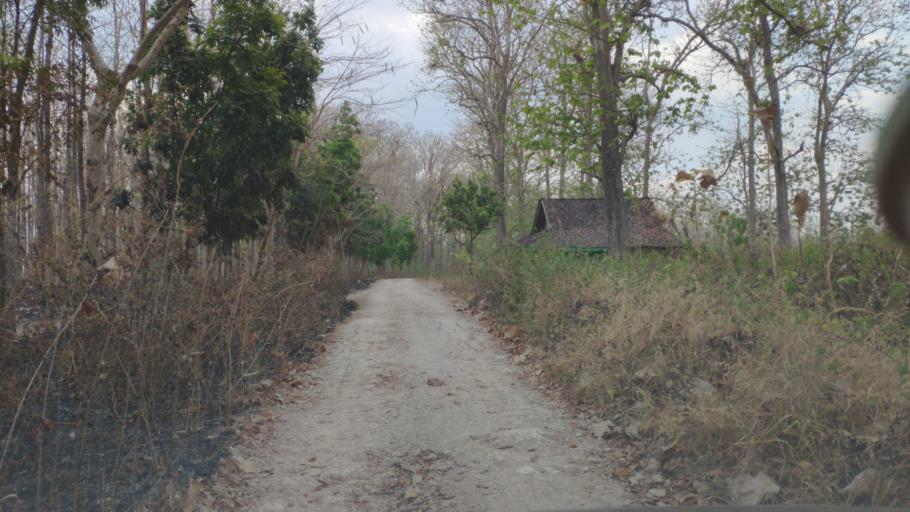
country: ID
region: Central Java
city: Randublatung
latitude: -7.3058
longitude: 111.3523
